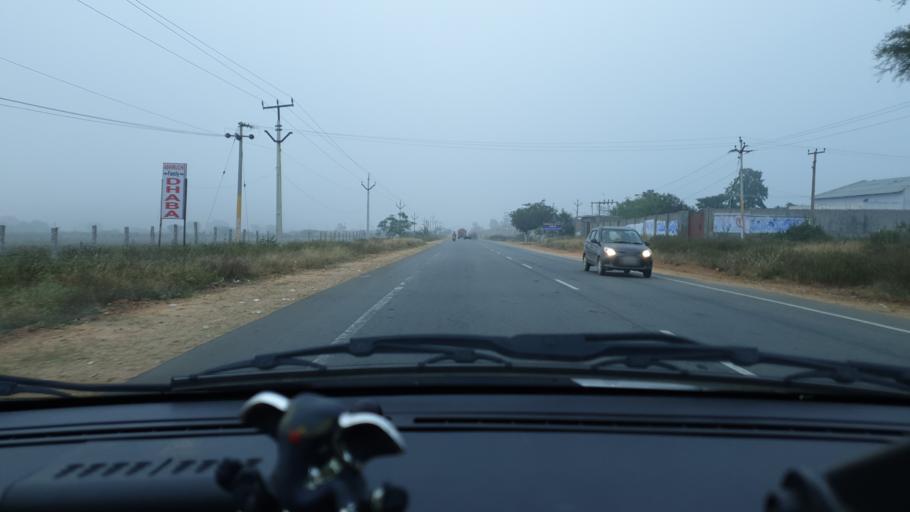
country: IN
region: Telangana
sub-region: Mahbubnagar
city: Farrukhnagar
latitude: 16.9197
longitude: 78.5272
